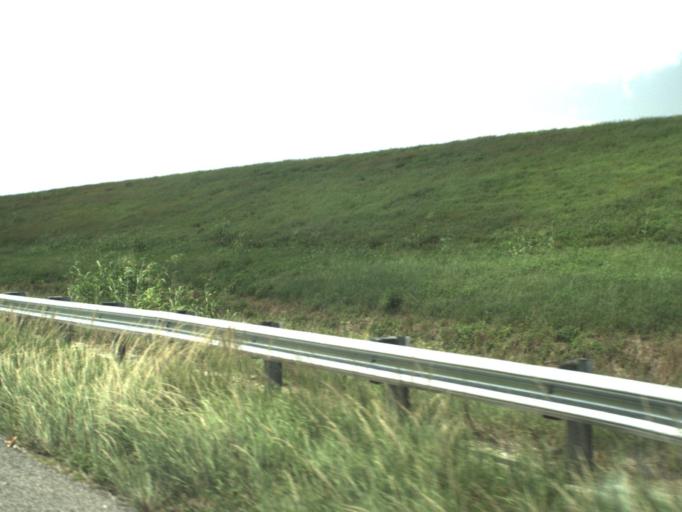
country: US
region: Florida
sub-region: Hendry County
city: Clewiston
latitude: 26.7335
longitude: -80.8643
